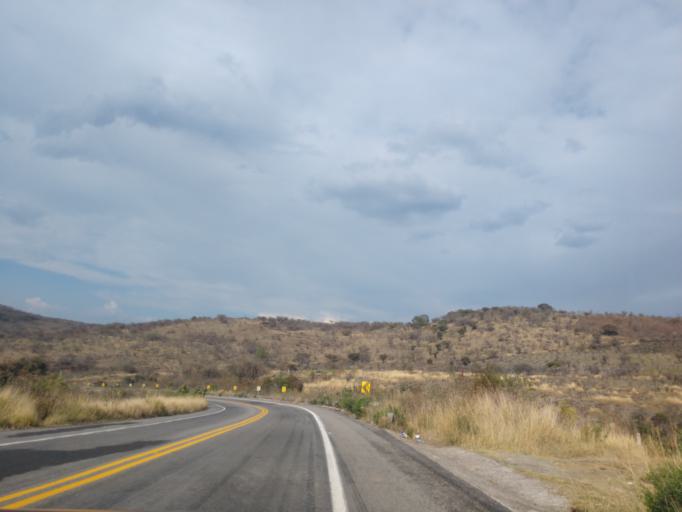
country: MX
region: Jalisco
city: La Manzanilla de la Paz
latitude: 20.0822
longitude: -103.1661
